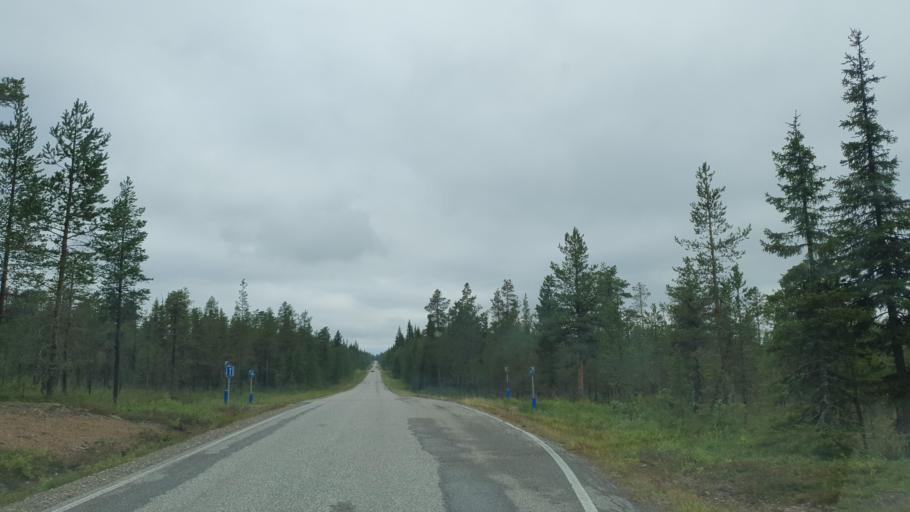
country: FI
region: Lapland
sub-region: Tunturi-Lappi
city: Muonio
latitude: 67.7960
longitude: 24.0846
